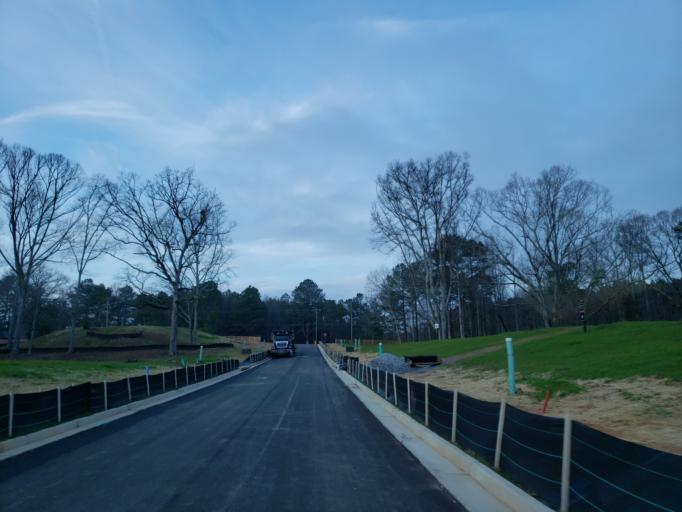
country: US
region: Georgia
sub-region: Cherokee County
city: Ball Ground
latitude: 34.2382
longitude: -84.3391
